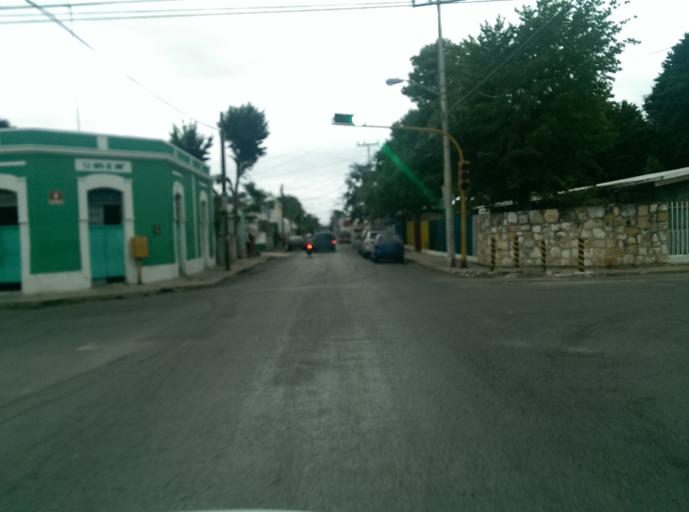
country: MX
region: Yucatan
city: Merida
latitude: 20.9780
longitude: -89.6358
